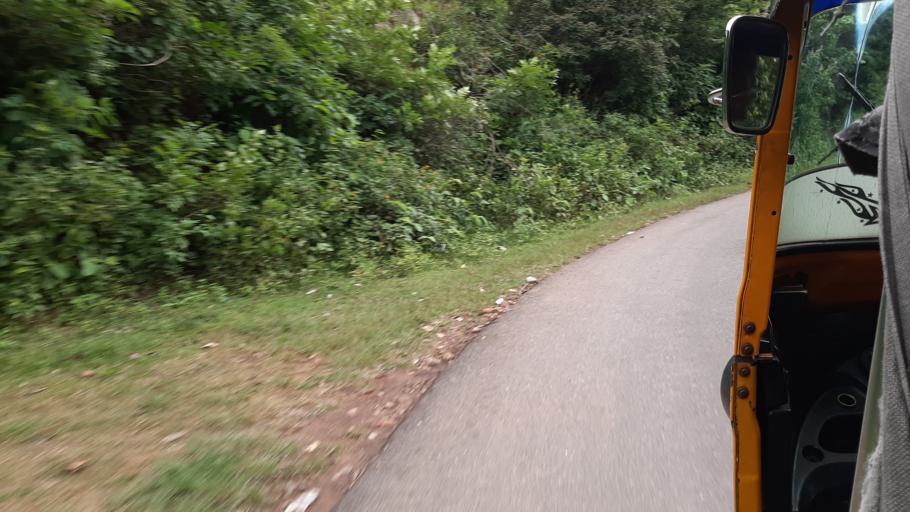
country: IN
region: Andhra Pradesh
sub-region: Vizianagaram District
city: Salur
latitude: 18.2429
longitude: 83.0261
